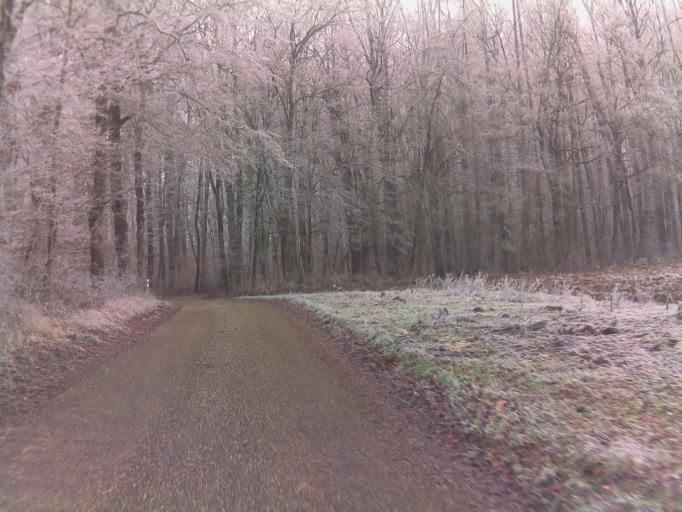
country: DE
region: Baden-Wuerttemberg
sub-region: Regierungsbezirk Stuttgart
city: Boxberg
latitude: 49.5194
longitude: 9.6506
